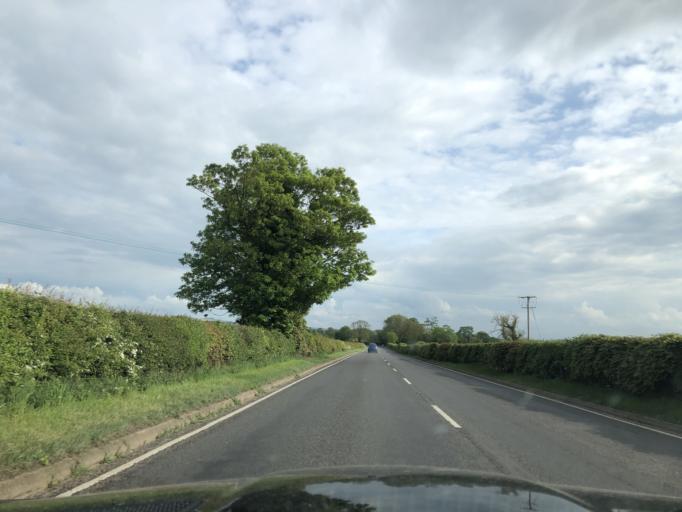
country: GB
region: England
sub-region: Warwickshire
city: Shipston on Stour
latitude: 52.1177
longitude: -1.6199
